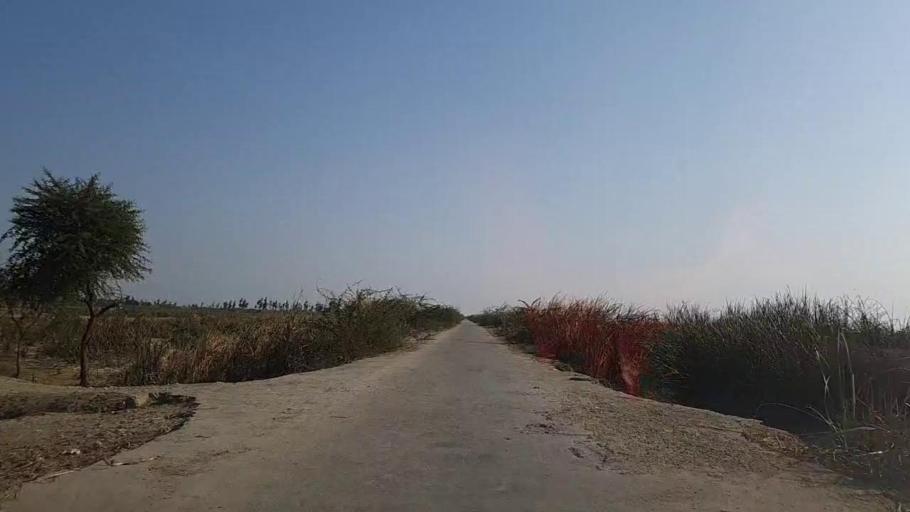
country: PK
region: Sindh
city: Sanghar
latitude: 25.9414
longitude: 69.0540
